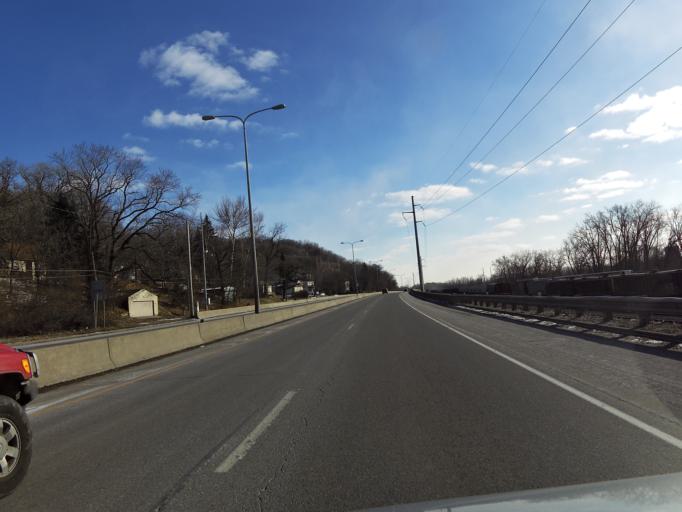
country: US
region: Minnesota
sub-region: Dakota County
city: South Saint Paul
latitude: 44.9174
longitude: -93.0156
